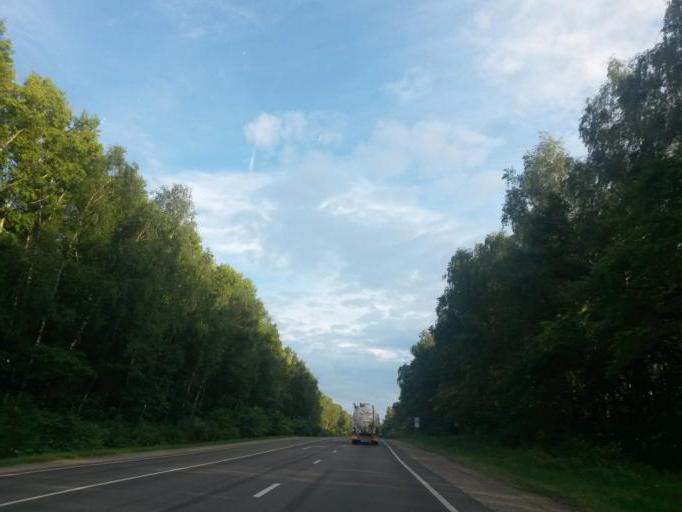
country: RU
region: Moskovskaya
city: Barybino
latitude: 55.2121
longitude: 37.8679
